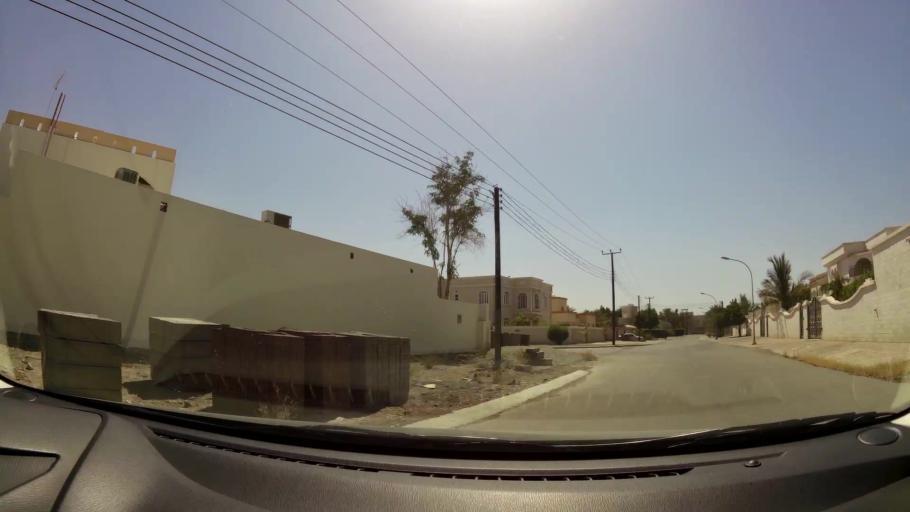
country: OM
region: Muhafazat Masqat
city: As Sib al Jadidah
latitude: 23.6355
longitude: 58.2219
